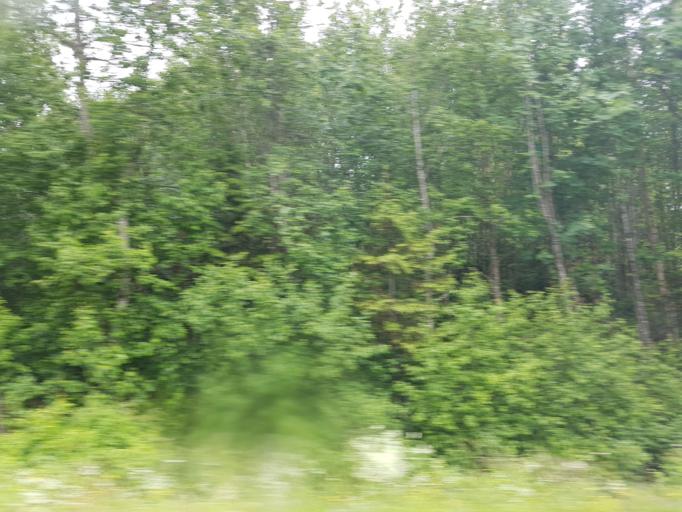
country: NO
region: Sor-Trondelag
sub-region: Selbu
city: Mebonden
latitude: 63.3701
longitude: 11.0712
